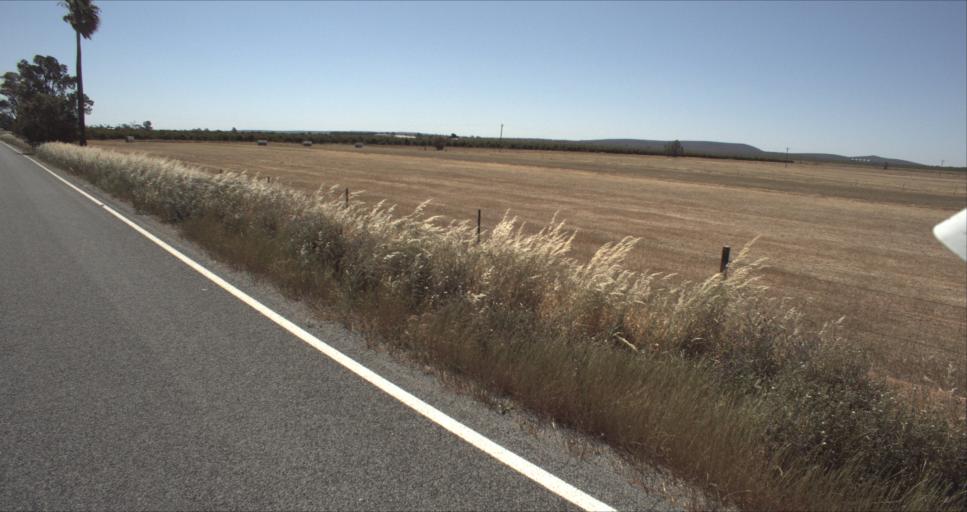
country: AU
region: New South Wales
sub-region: Leeton
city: Leeton
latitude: -34.5199
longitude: 146.4379
